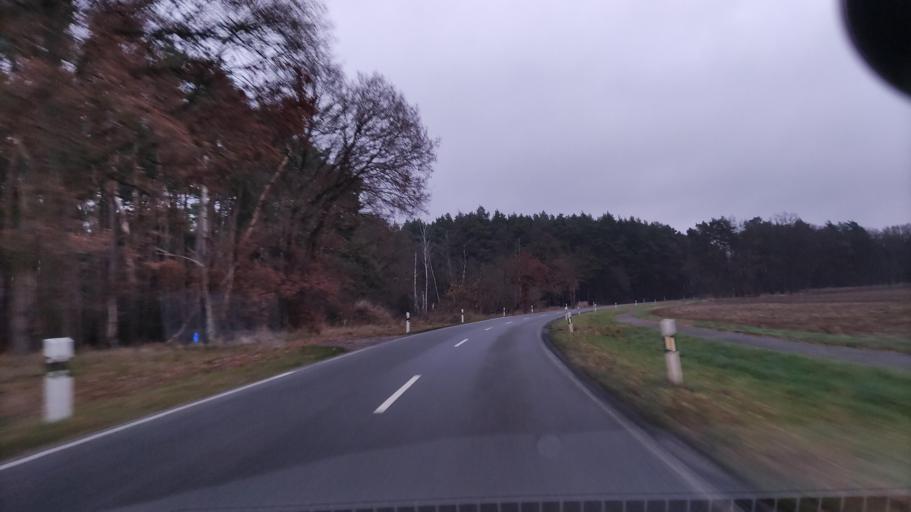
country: DE
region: Lower Saxony
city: Waddeweitz
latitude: 52.9934
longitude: 10.9851
